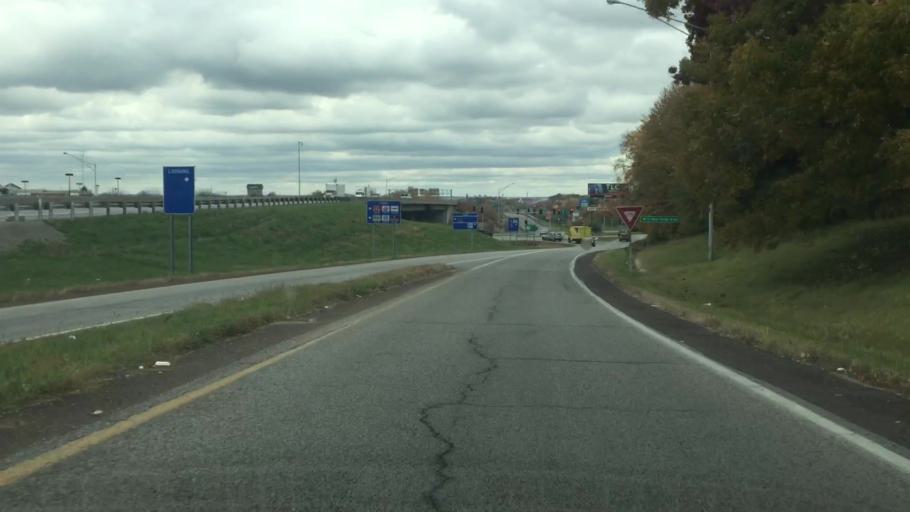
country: US
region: Missouri
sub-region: Jackson County
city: Raytown
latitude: 39.0475
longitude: -94.4410
